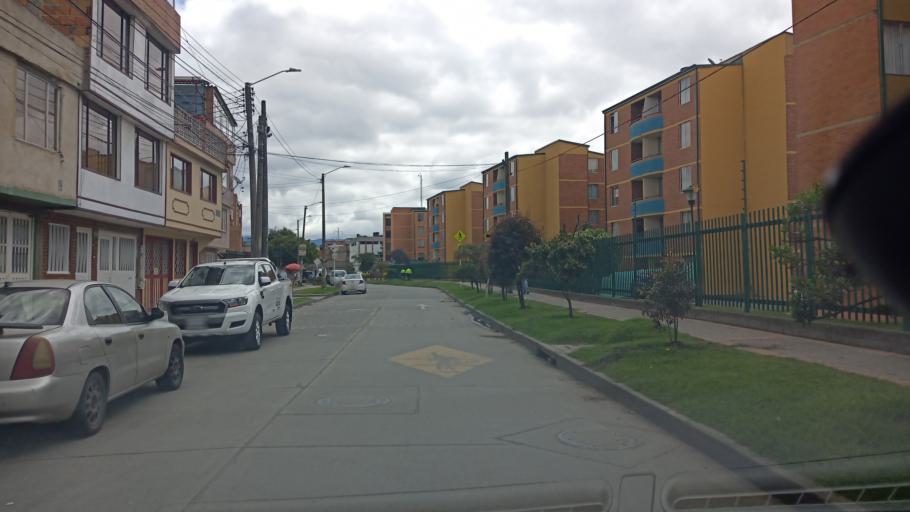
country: CO
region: Cundinamarca
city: Funza
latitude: 4.6691
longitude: -74.1496
